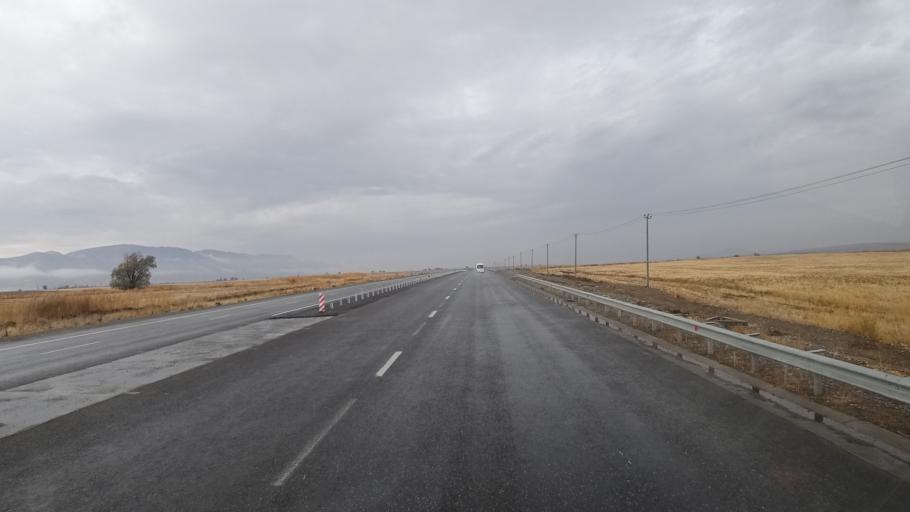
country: KZ
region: Ongtustik Qazaqstan
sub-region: Tulkibas Audany
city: Zhabagly
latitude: 42.5071
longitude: 70.4386
